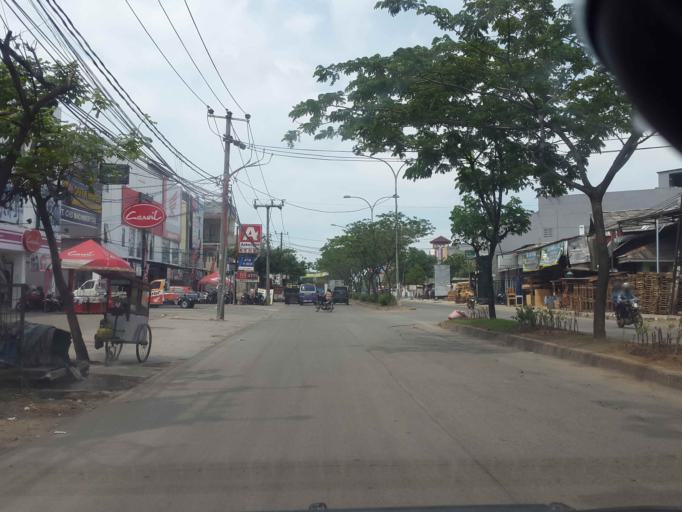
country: ID
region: Banten
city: Tangerang
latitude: -6.1517
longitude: 106.6744
